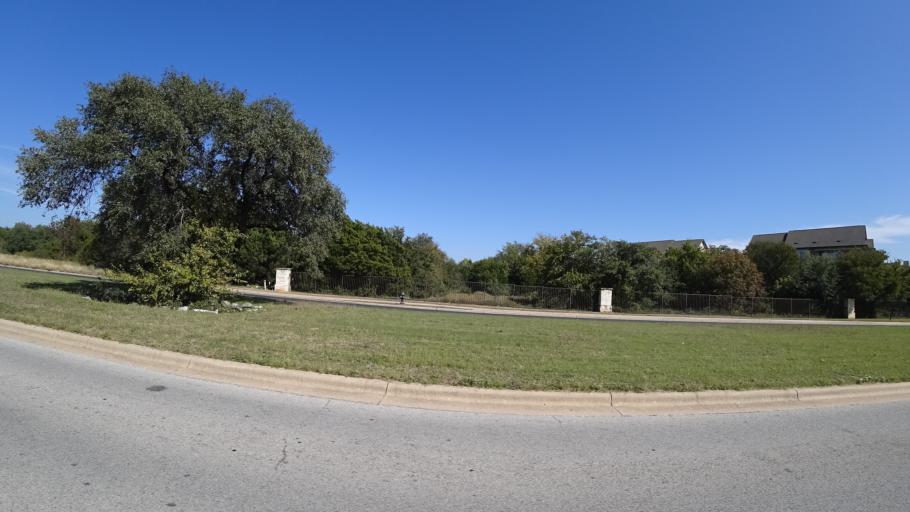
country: US
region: Texas
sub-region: Travis County
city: Shady Hollow
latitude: 30.1908
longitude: -97.8577
